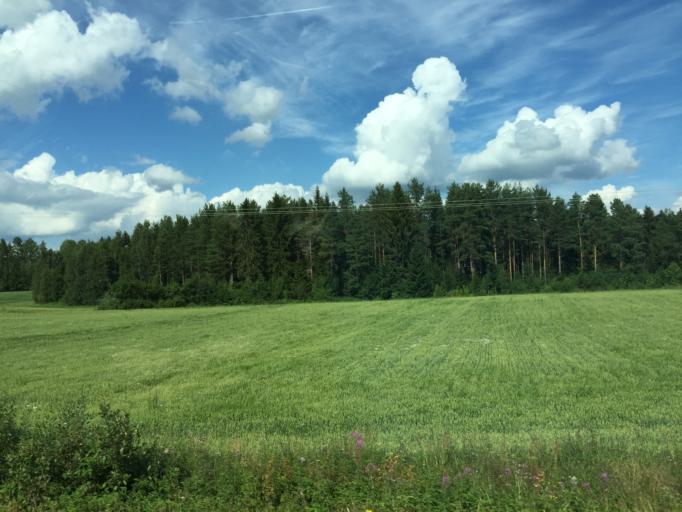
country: SE
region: Gaevleborg
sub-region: Soderhamns Kommun
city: Soderhamn
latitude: 61.1642
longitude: 16.8582
